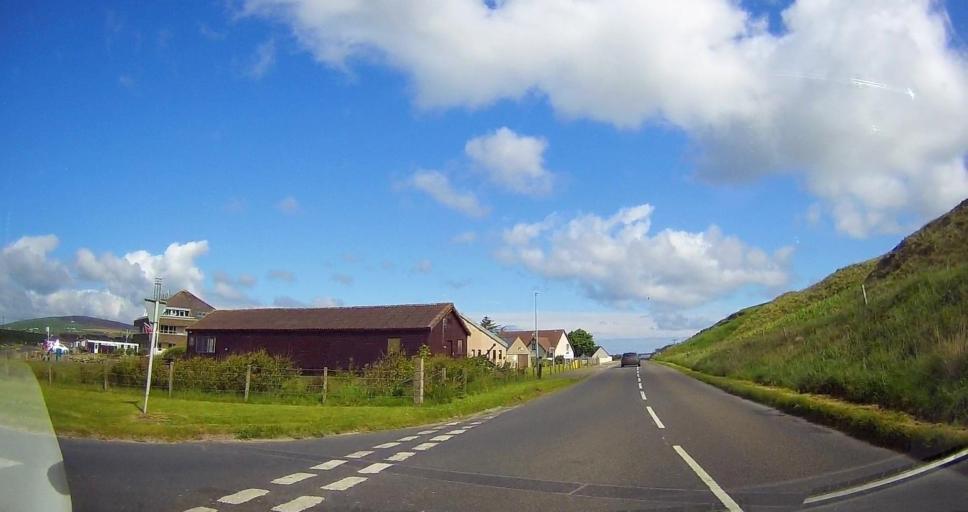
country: GB
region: Scotland
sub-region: Orkney Islands
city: Orkney
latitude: 58.9598
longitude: -2.9688
